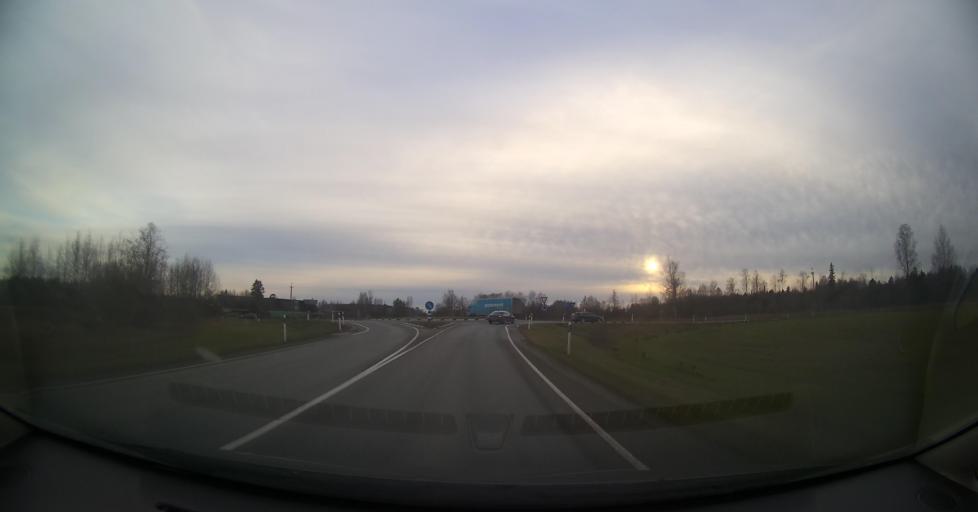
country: EE
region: Ida-Virumaa
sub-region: Johvi vald
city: Johvi
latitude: 59.3397
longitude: 27.4693
